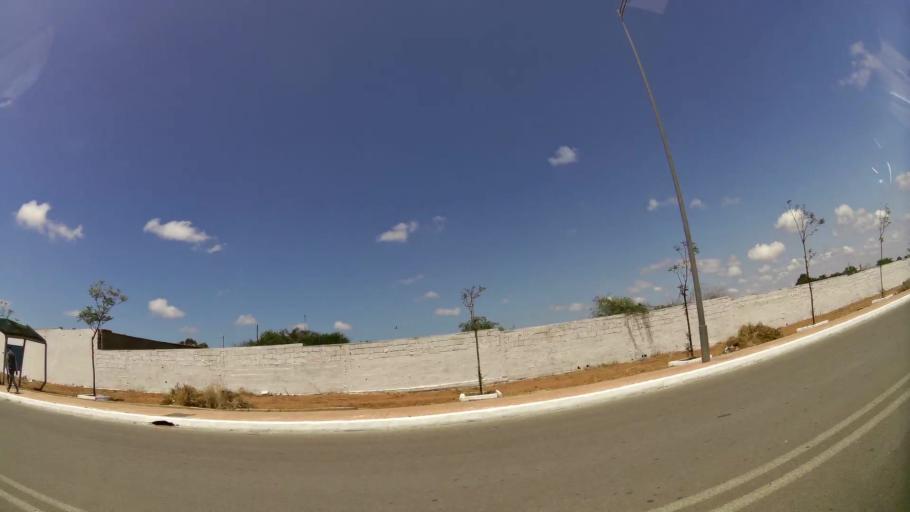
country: MA
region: Gharb-Chrarda-Beni Hssen
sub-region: Kenitra Province
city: Kenitra
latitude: 34.2489
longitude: -6.5677
